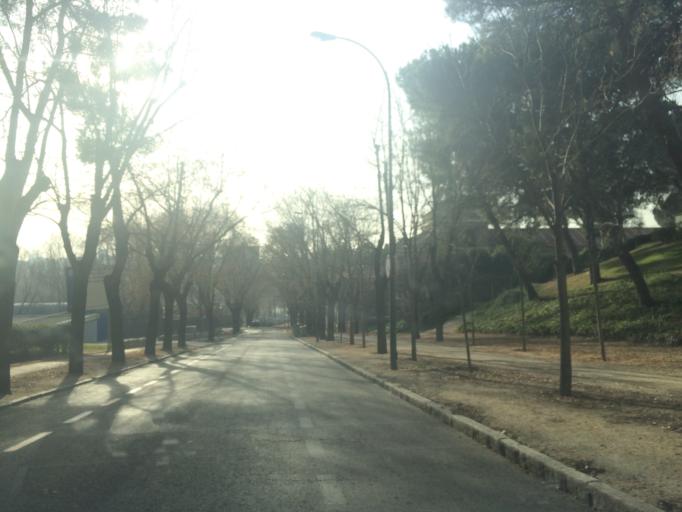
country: ES
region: Madrid
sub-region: Provincia de Madrid
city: Moncloa-Aravaca
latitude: 40.4274
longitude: -3.7231
